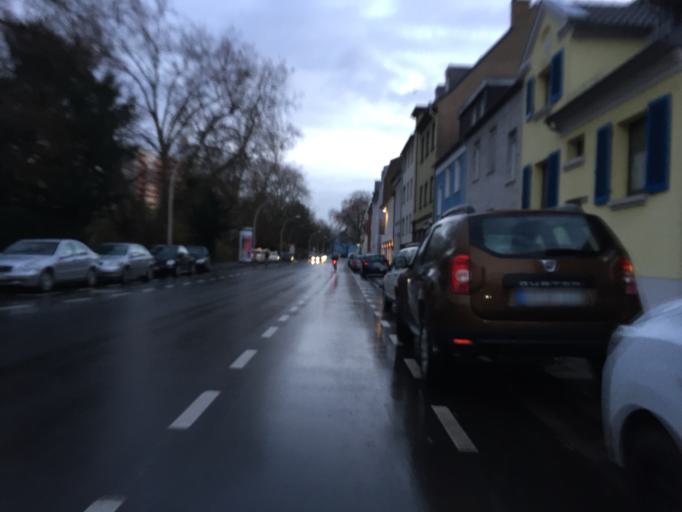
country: DE
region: North Rhine-Westphalia
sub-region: Regierungsbezirk Koln
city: Bonn
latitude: 50.7498
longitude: 7.0977
